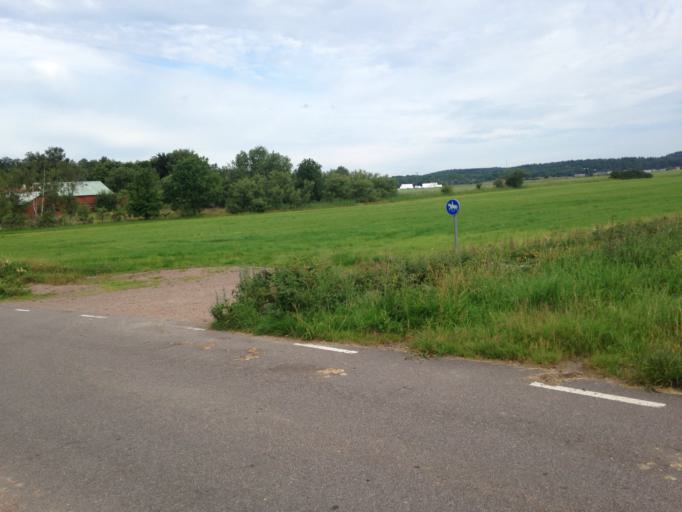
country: SE
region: Vaestra Goetaland
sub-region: Goteborg
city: Majorna
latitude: 57.8024
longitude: 11.8853
